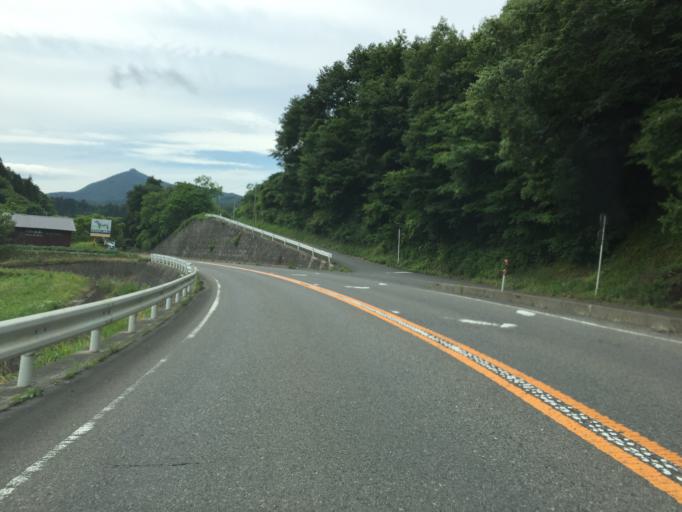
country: JP
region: Fukushima
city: Funehikimachi-funehiki
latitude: 37.4580
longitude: 140.7299
